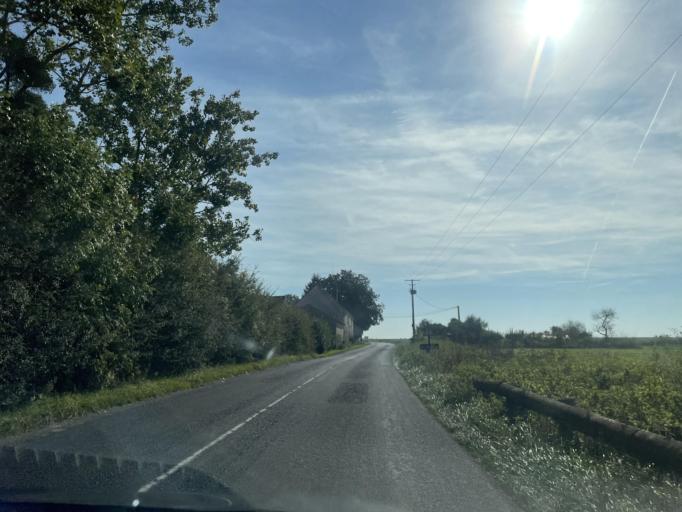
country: FR
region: Ile-de-France
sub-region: Departement de Seine-et-Marne
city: Coulommiers
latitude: 48.8777
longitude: 3.0782
